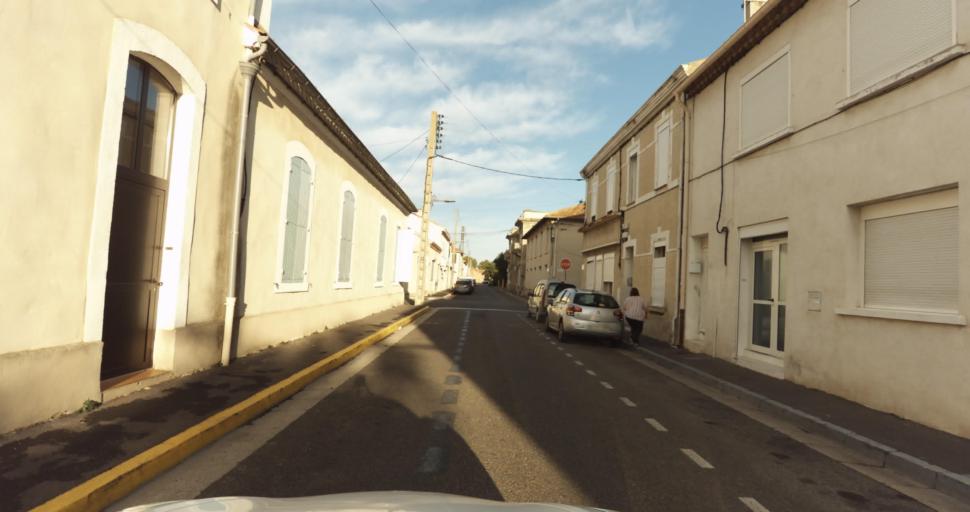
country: FR
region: Provence-Alpes-Cote d'Azur
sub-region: Departement des Bouches-du-Rhone
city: Miramas
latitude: 43.5823
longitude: 4.9993
